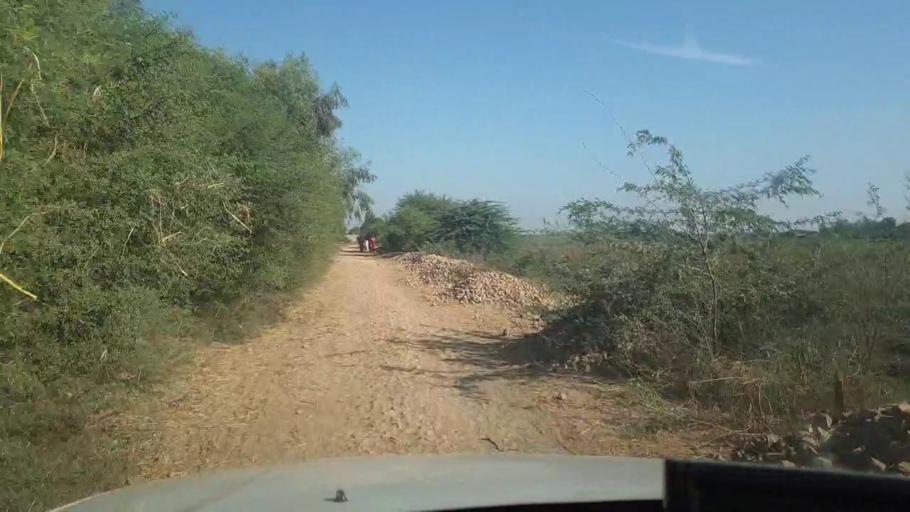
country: PK
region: Sindh
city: Mirpur Sakro
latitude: 24.4963
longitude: 67.6231
